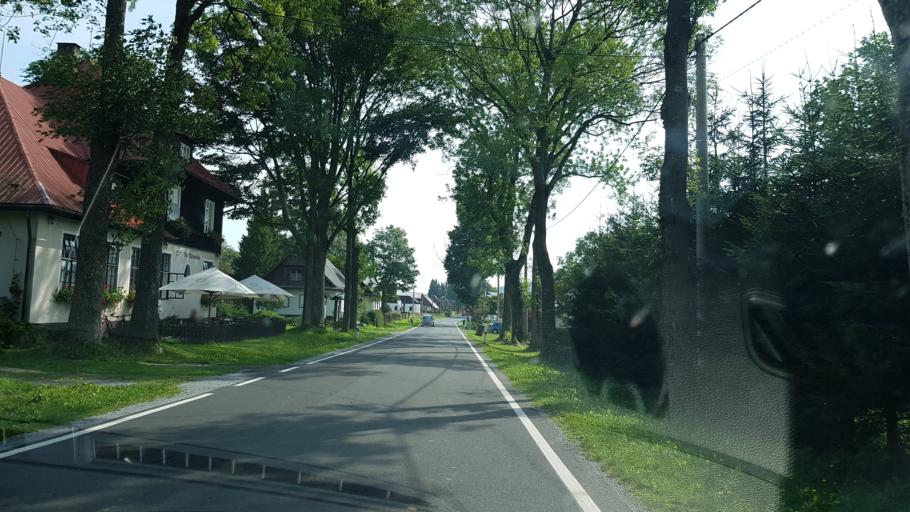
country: CZ
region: Olomoucky
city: Mikulovice
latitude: 50.2297
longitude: 17.3093
